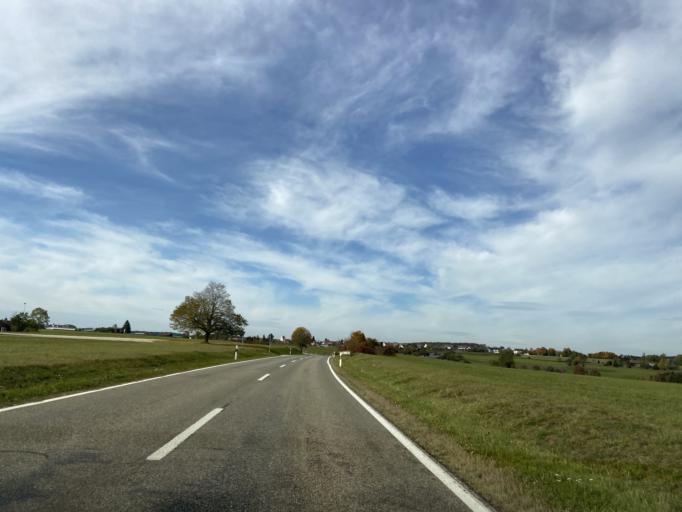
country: DE
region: Baden-Wuerttemberg
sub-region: Tuebingen Region
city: Leibertingen
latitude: 48.0539
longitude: 9.0658
